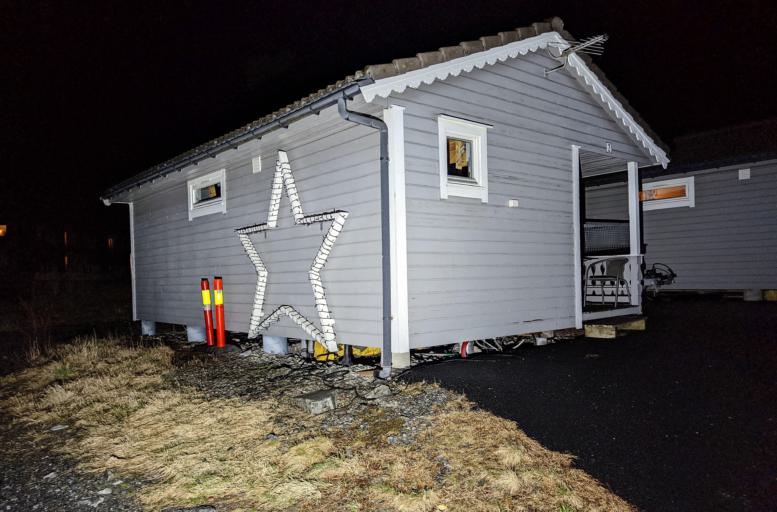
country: NO
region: Rogaland
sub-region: Vindafjord
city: Olen
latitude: 59.8582
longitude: 5.7543
